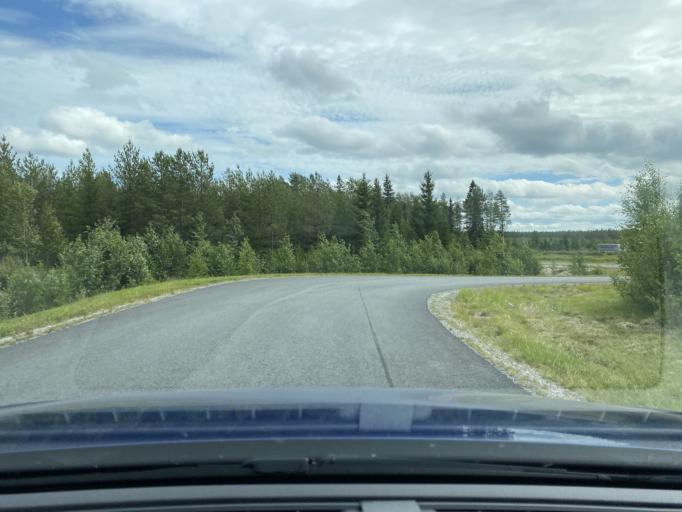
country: FI
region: Southern Ostrobothnia
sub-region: Seinaejoki
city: Jurva
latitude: 62.6250
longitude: 22.0306
